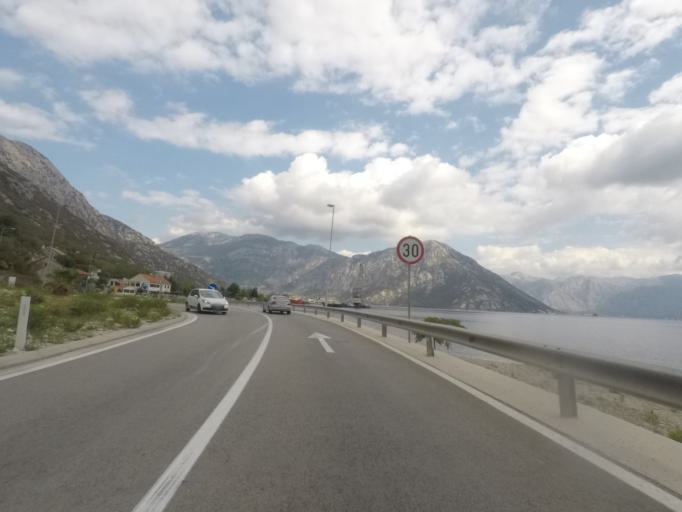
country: ME
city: Lipci
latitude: 42.4952
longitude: 18.6542
